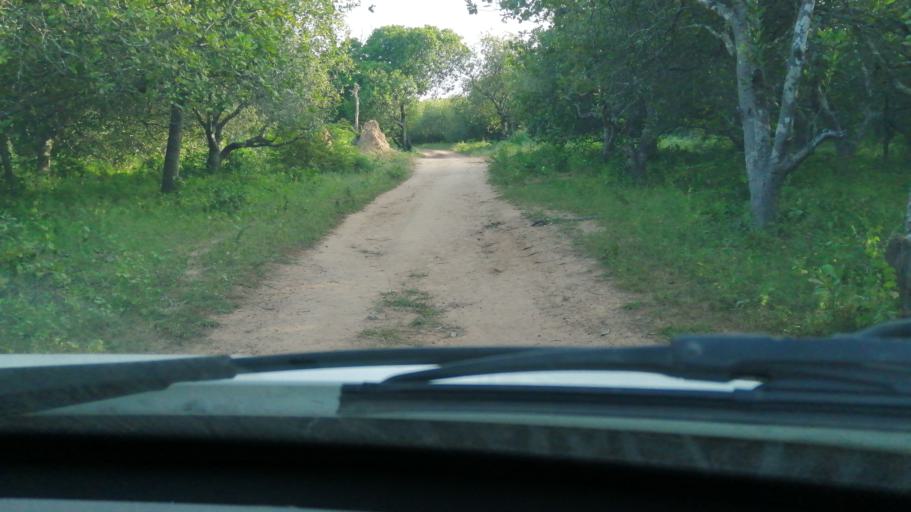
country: GW
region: Oio
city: Mansoa
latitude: 11.9992
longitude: -15.4719
